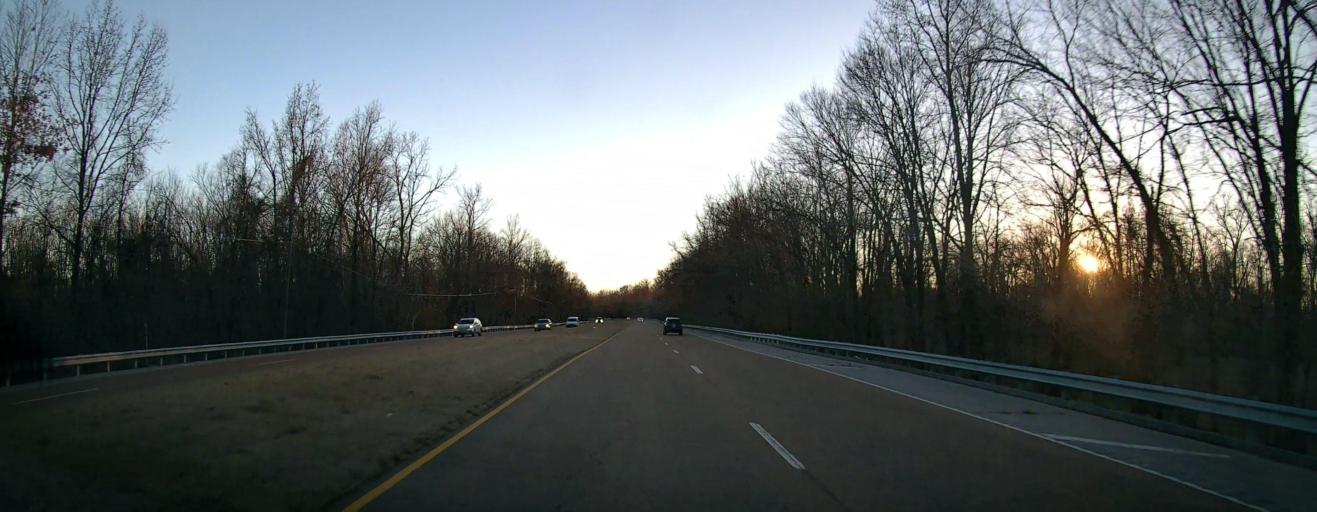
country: US
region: Tennessee
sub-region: Shelby County
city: Millington
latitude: 35.2827
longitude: -89.8849
